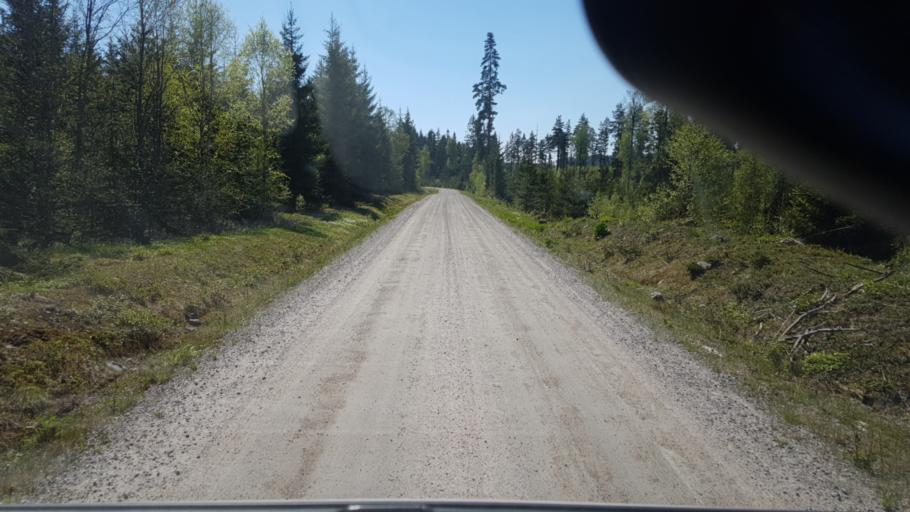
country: SE
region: Vaermland
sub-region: Sunne Kommun
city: Sunne
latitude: 59.8253
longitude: 12.8437
